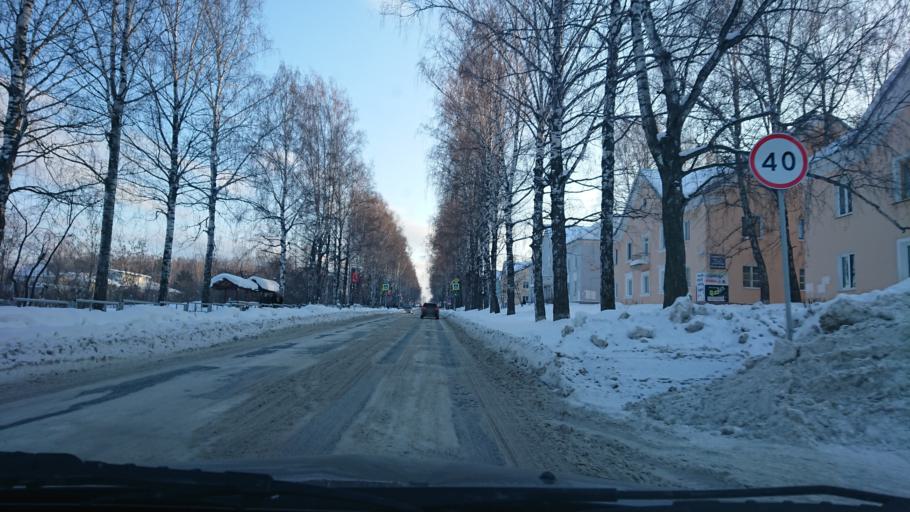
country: RU
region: Sverdlovsk
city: Degtyarsk
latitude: 56.6976
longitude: 60.0877
